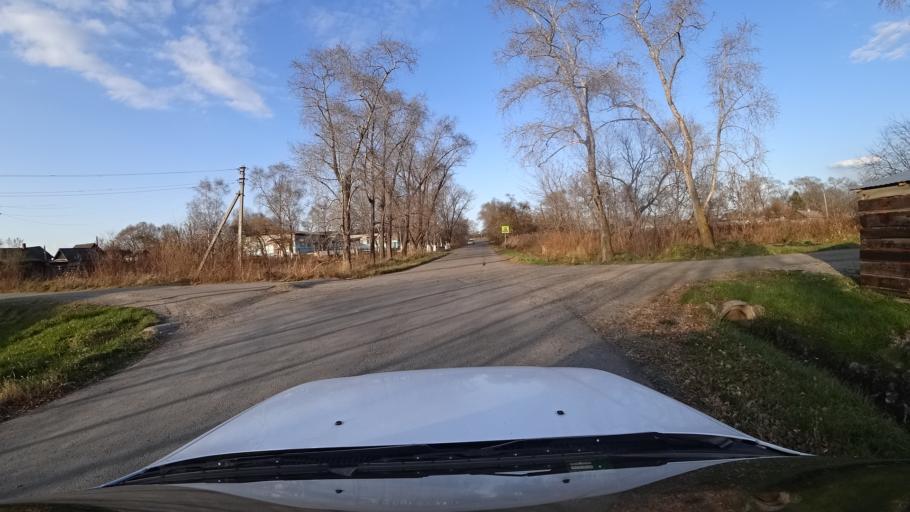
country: RU
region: Primorskiy
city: Lazo
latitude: 45.8273
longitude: 133.6143
